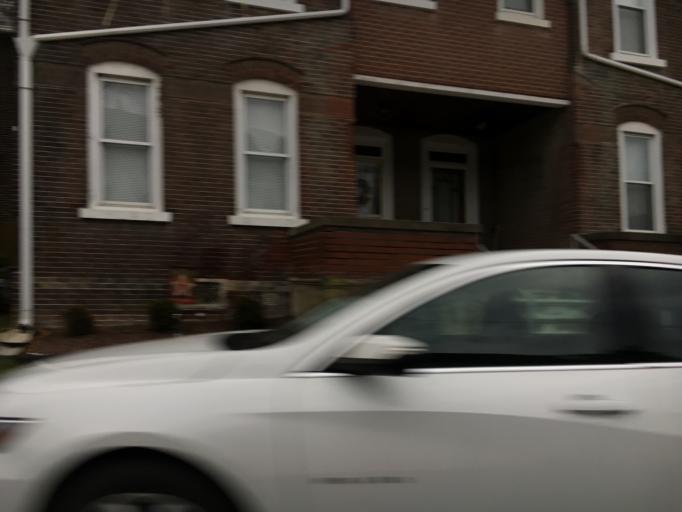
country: US
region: Pennsylvania
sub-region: Northampton County
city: Northampton
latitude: 40.6929
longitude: -75.5001
